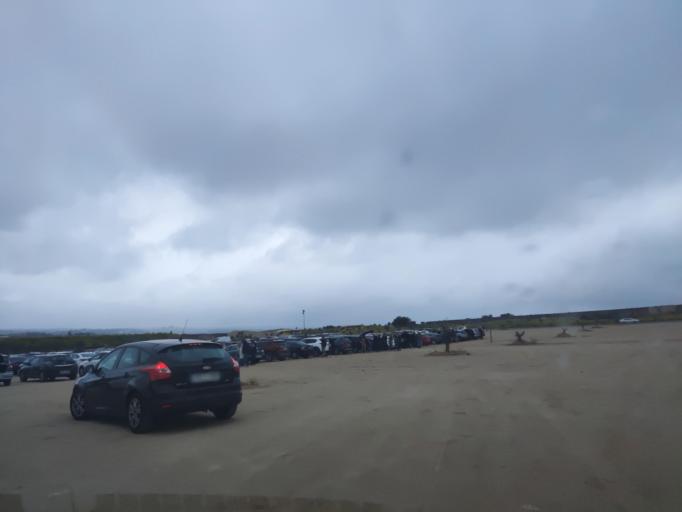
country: ES
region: Castille-La Mancha
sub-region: Province of Toledo
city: Layos
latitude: 39.8388
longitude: -4.0865
